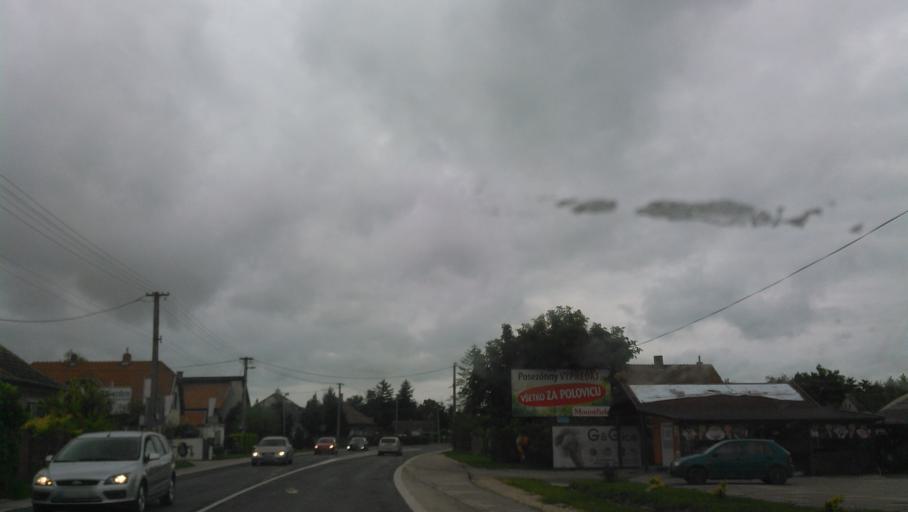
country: SK
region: Trnavsky
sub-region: Okres Dunajska Streda
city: Velky Meder
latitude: 47.9406
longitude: 17.7171
